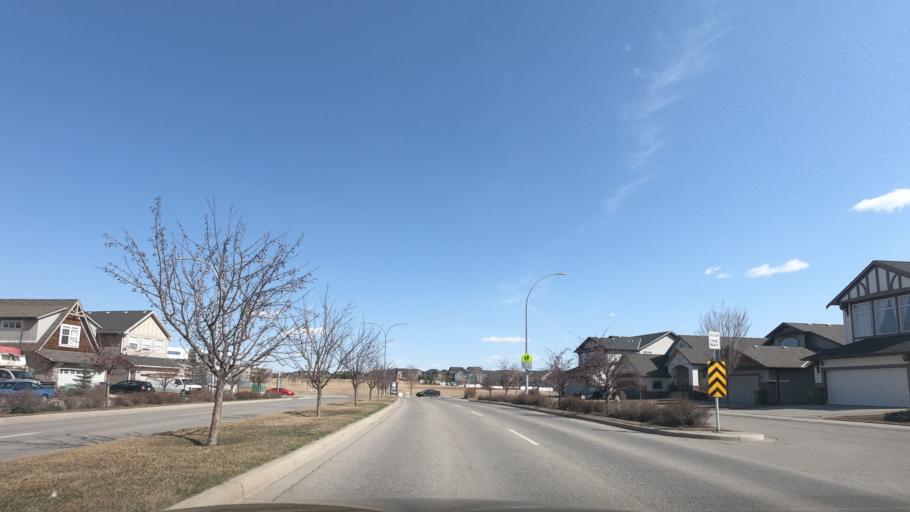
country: CA
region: Alberta
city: Airdrie
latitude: 51.2663
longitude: -113.9857
